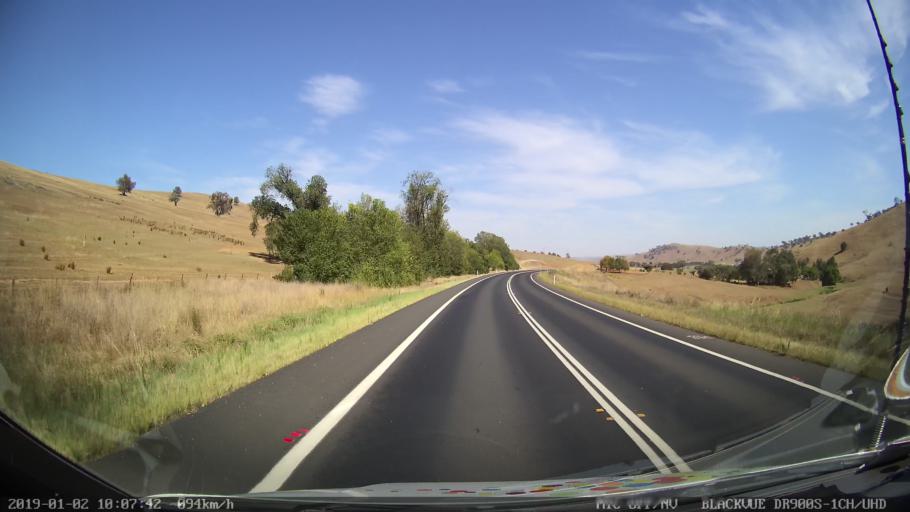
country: AU
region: New South Wales
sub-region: Gundagai
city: Gundagai
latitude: -35.1360
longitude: 148.1092
